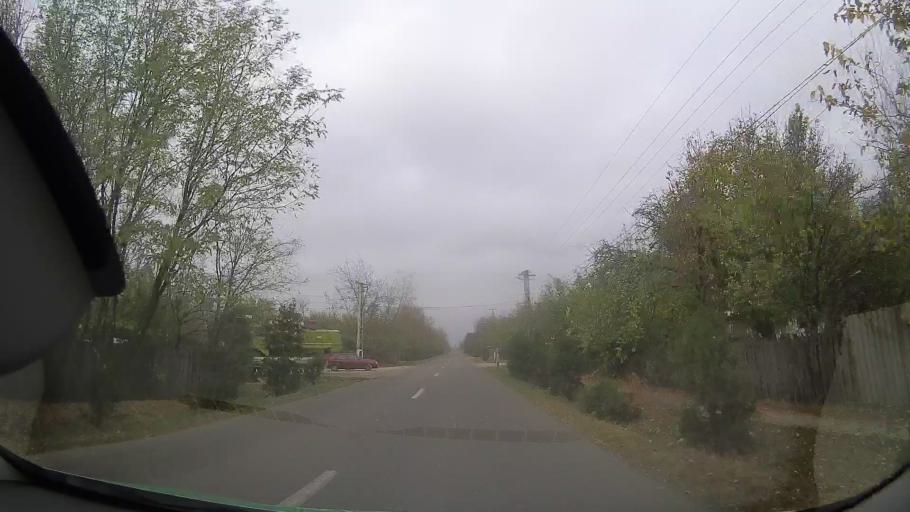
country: RO
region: Buzau
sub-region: Comuna Scutelnici
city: Scutelnici
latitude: 44.8807
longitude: 26.8766
